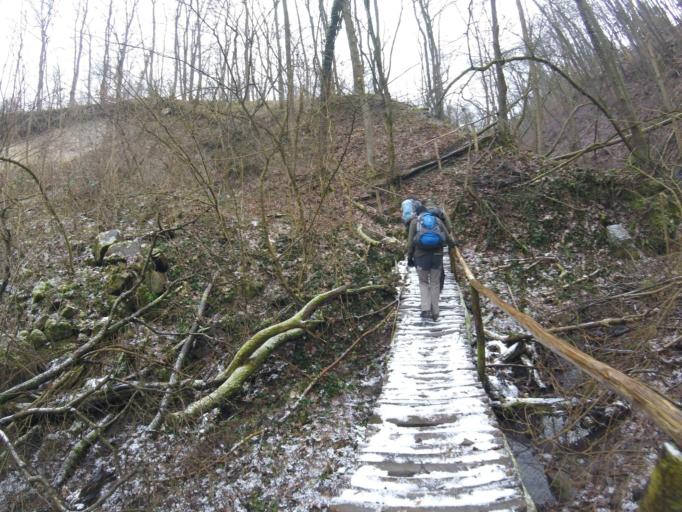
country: HU
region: Pest
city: Visegrad
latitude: 47.7703
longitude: 18.9862
